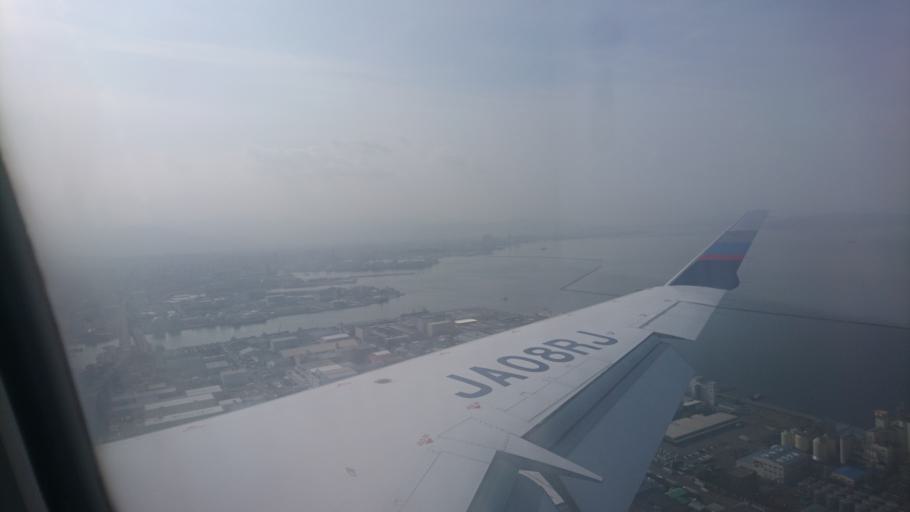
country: JP
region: Fukuoka
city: Fukuoka-shi
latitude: 33.6331
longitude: 130.4181
